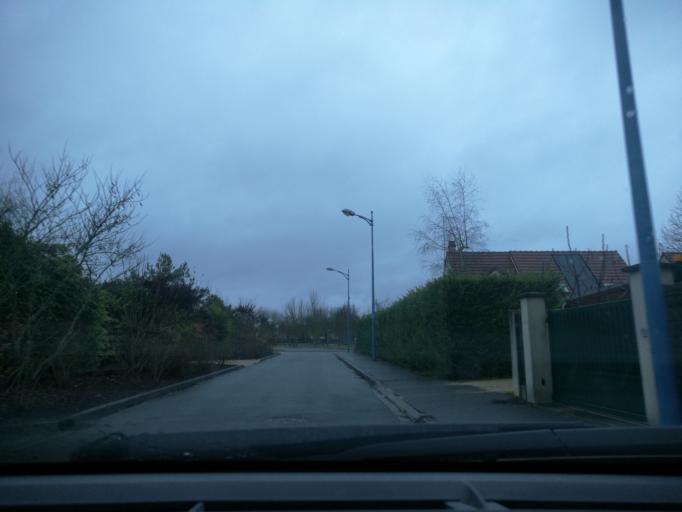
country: FR
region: Centre
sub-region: Departement du Loiret
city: Fleury-les-Aubrais
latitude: 47.9363
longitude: 1.9073
